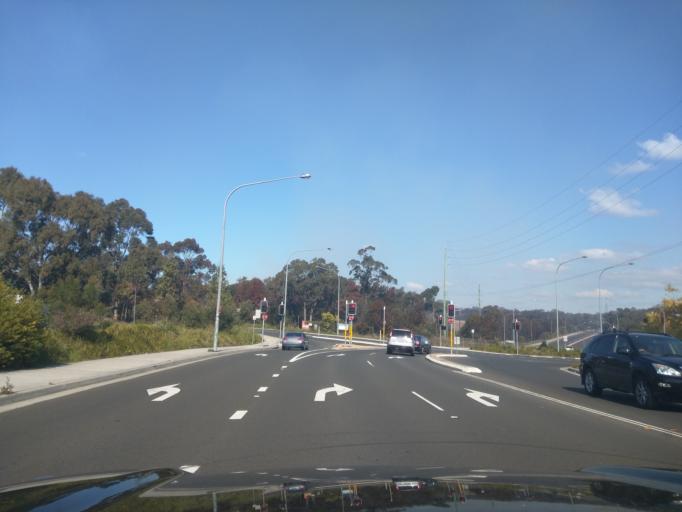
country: AU
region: New South Wales
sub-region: Sutherland Shire
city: Menai
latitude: -34.0325
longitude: 151.0057
